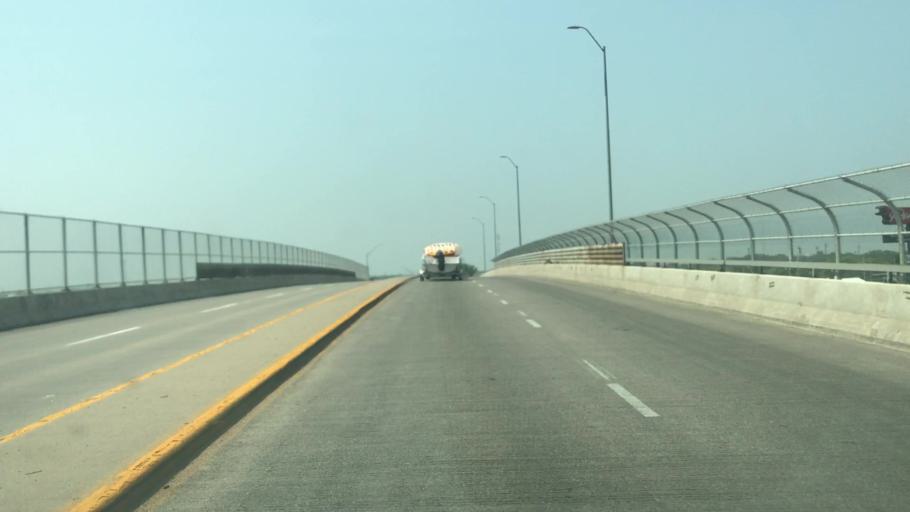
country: US
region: Nebraska
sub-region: Hall County
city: Grand Island
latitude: 40.9151
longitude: -98.3655
